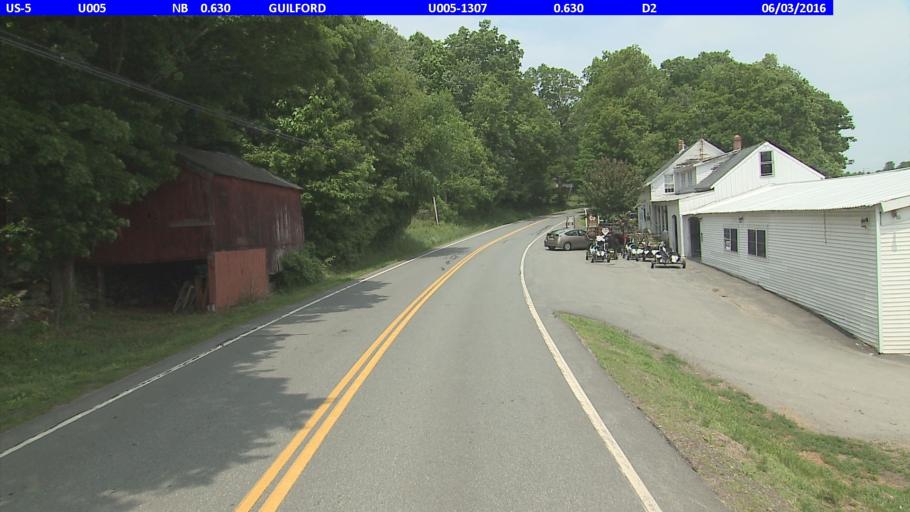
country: US
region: Massachusetts
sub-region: Franklin County
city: Bernardston
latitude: 42.7391
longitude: -72.5726
